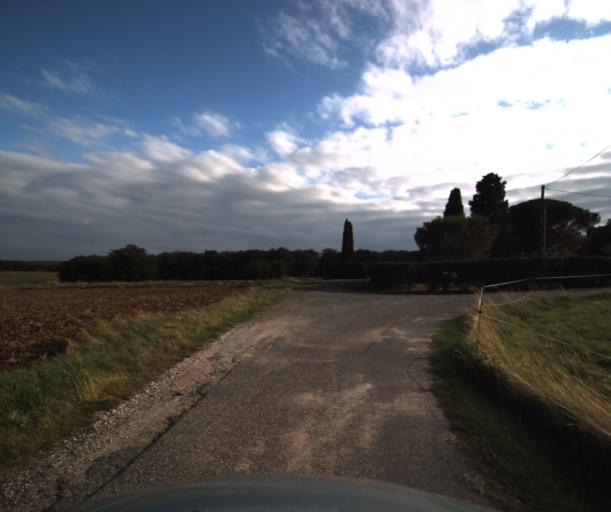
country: FR
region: Midi-Pyrenees
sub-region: Departement de la Haute-Garonne
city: Eaunes
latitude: 43.4297
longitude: 1.3339
